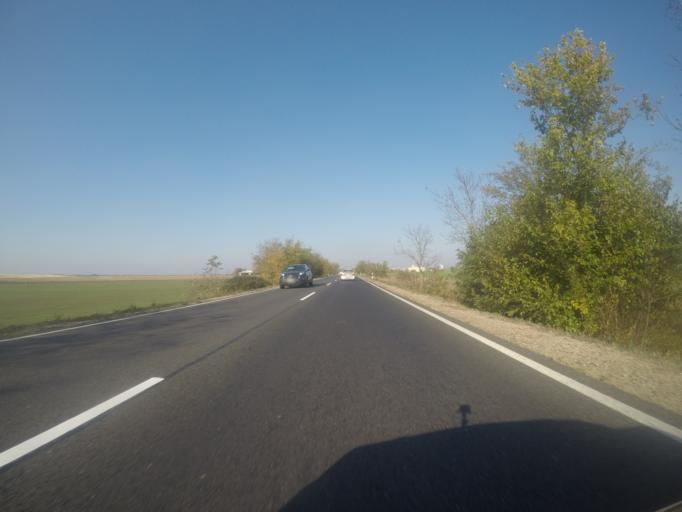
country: HU
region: Fejer
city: Baracs
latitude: 46.8902
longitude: 18.9204
